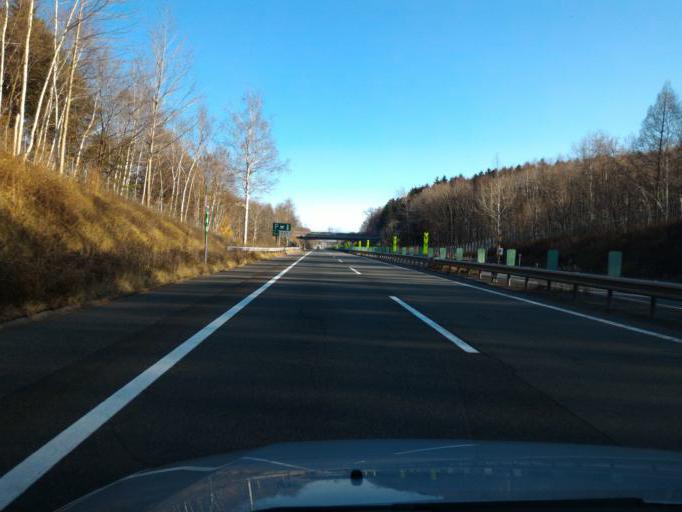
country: JP
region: Hokkaido
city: Iwamizawa
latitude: 43.1865
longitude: 141.7877
